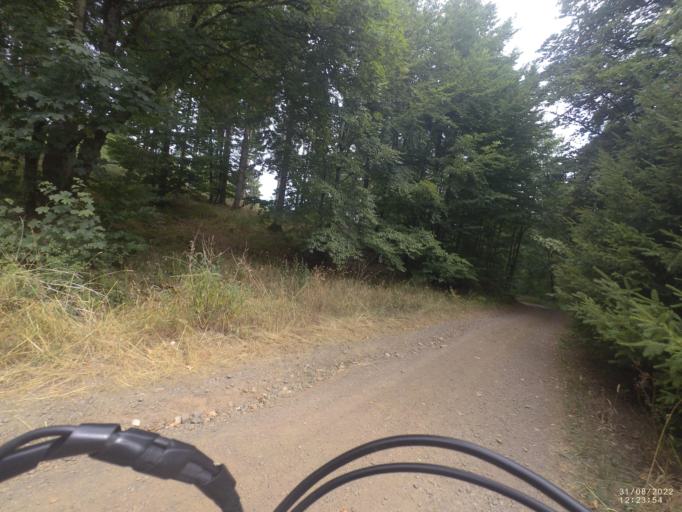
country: DE
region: Rheinland-Pfalz
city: Steffeln
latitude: 50.3068
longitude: 6.5559
